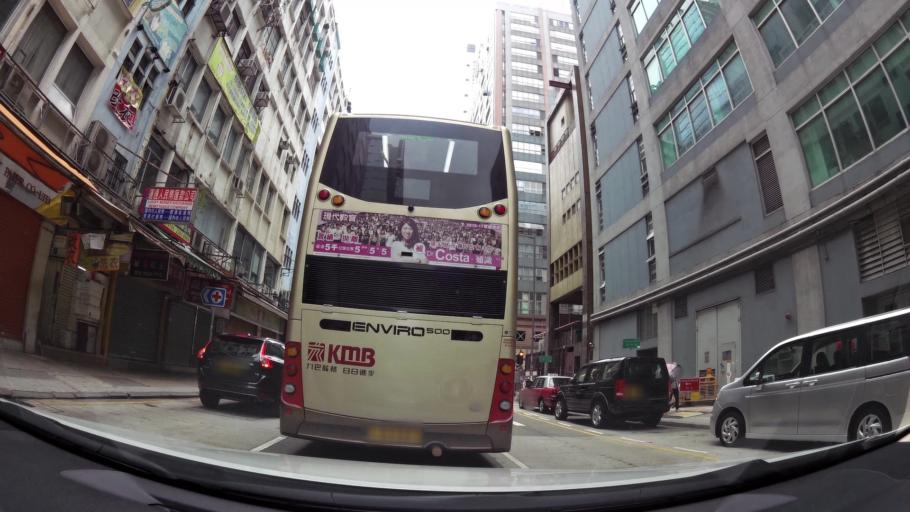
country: HK
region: Sham Shui Po
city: Sham Shui Po
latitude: 22.3384
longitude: 114.1488
